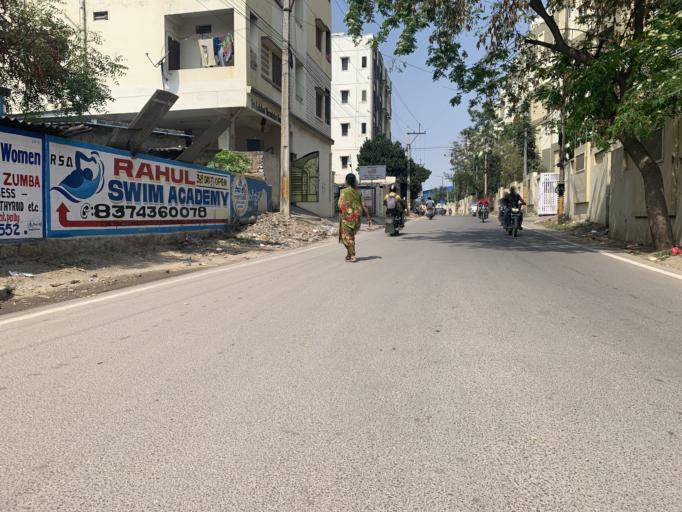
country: IN
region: Telangana
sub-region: Rangareddi
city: Kukatpalli
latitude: 17.4960
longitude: 78.4201
